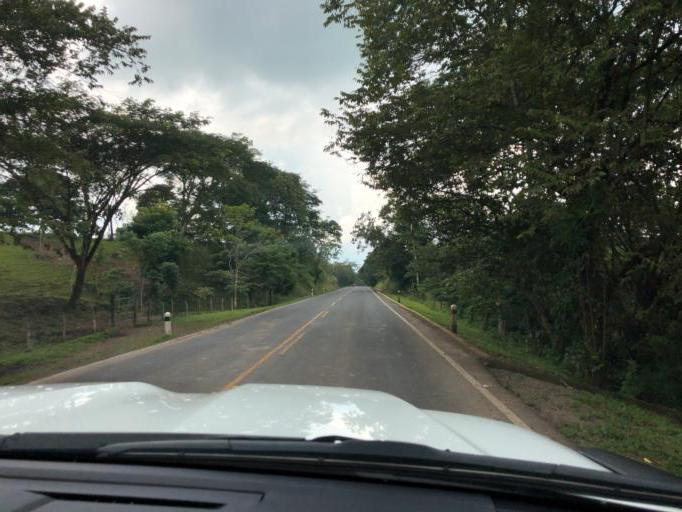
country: NI
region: Chontales
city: Villa Sandino
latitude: 11.9934
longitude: -84.8044
